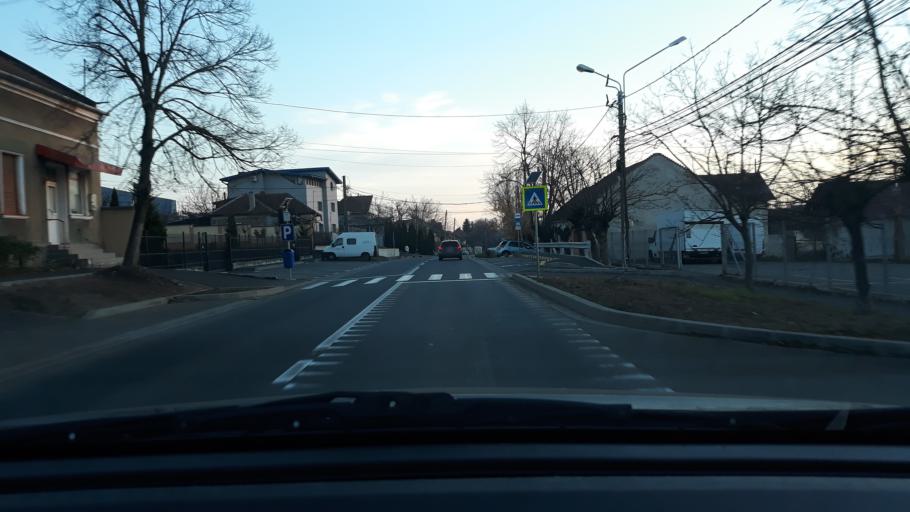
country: RO
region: Bihor
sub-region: Comuna Biharea
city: Oradea
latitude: 47.0858
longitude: 21.9269
